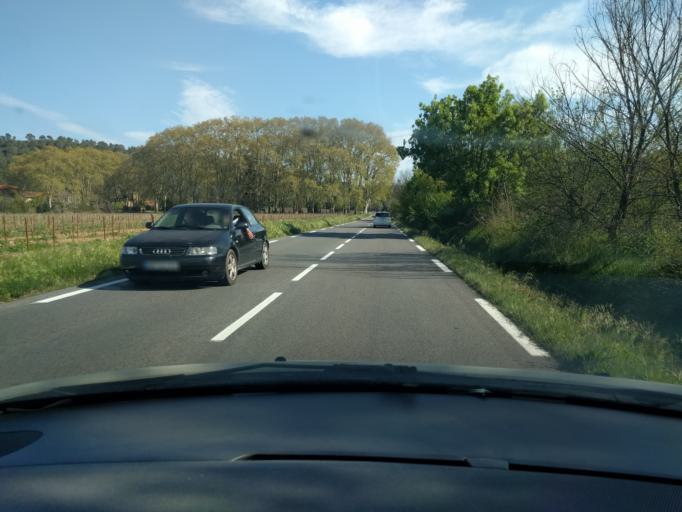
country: FR
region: Provence-Alpes-Cote d'Azur
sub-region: Departement du Var
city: Hyeres
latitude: 43.1605
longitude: 6.1257
